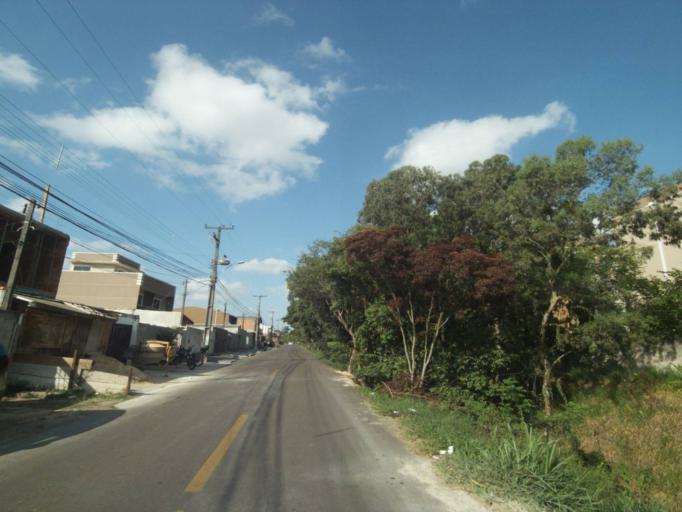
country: BR
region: Parana
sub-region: Curitiba
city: Curitiba
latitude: -25.5107
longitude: -49.3302
